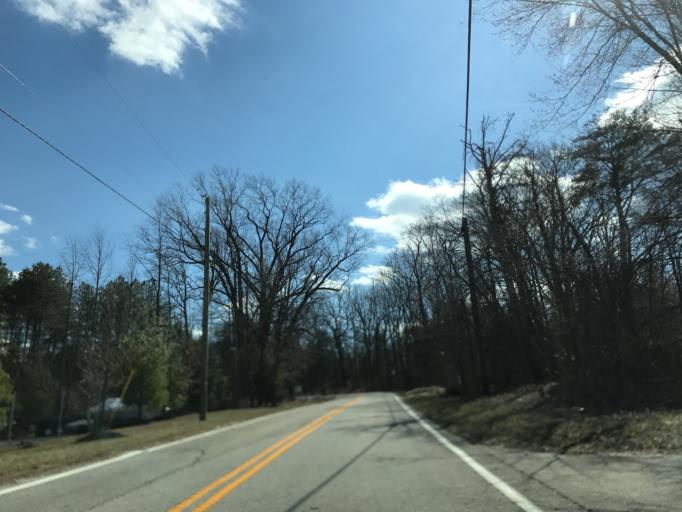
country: US
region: Maryland
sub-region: Anne Arundel County
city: Pasadena
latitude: 39.1325
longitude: -76.5809
